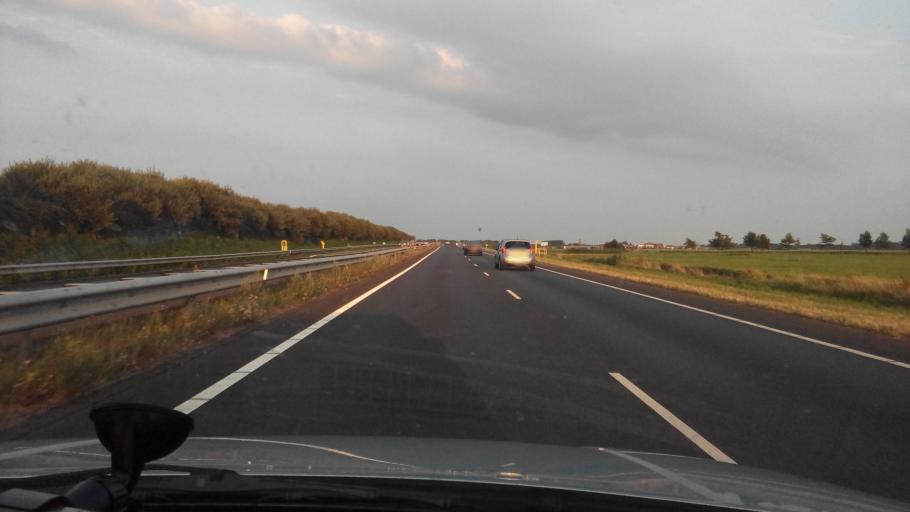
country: NL
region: South Holland
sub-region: Bodegraven-Reeuwijk
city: Bodegraven
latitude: 52.1033
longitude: 4.7123
